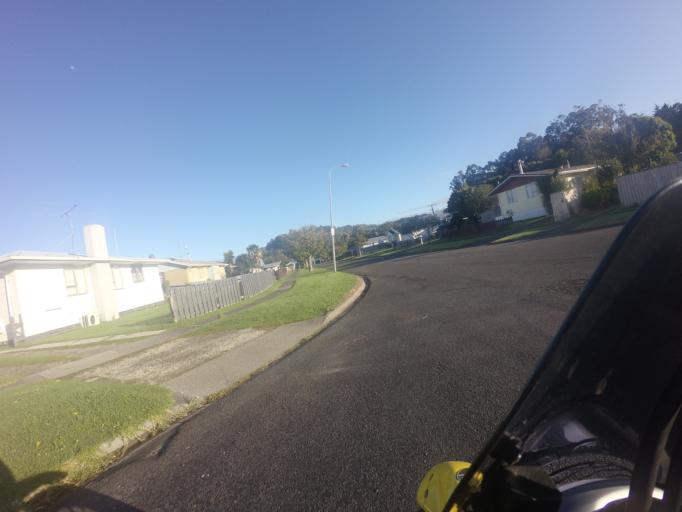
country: NZ
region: Gisborne
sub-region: Gisborne District
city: Gisborne
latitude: -38.6678
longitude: 178.0517
